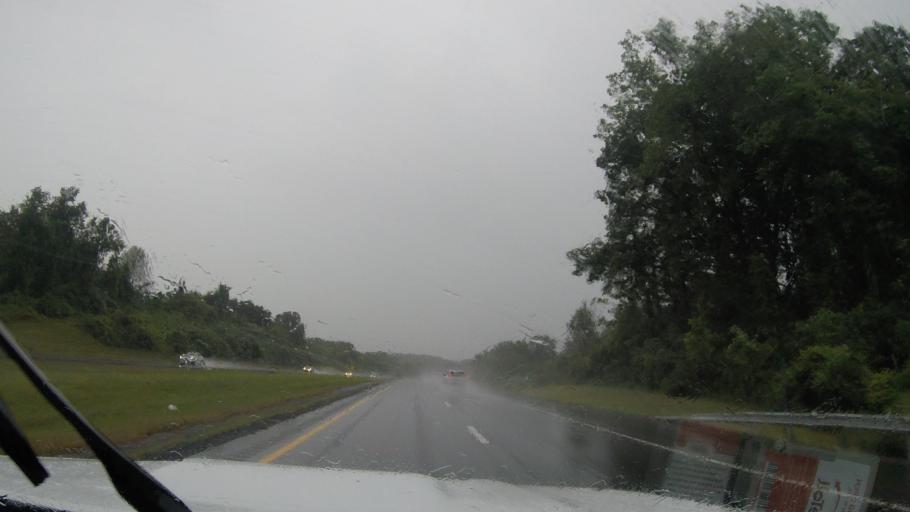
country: US
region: New York
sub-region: Ontario County
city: Geneva
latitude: 42.9584
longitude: -76.9533
